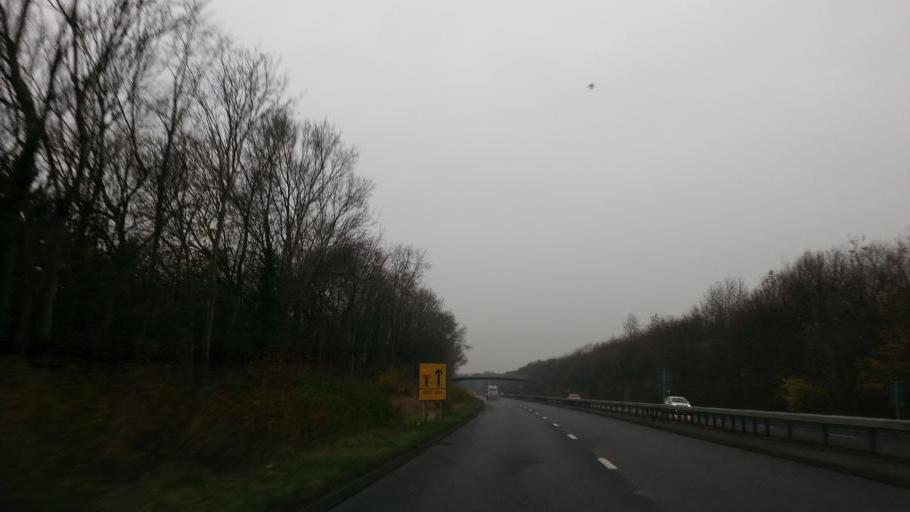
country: GB
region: England
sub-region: Peterborough
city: Castor
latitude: 52.5472
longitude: -0.3083
